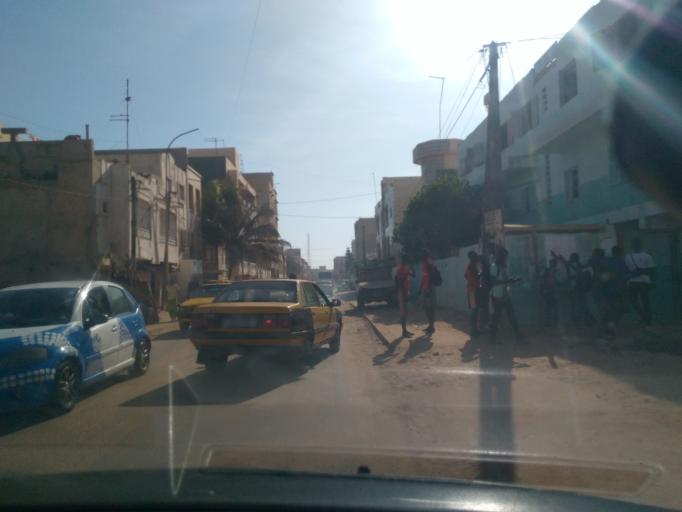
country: SN
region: Dakar
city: Grand Dakar
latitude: 14.7632
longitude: -17.4450
